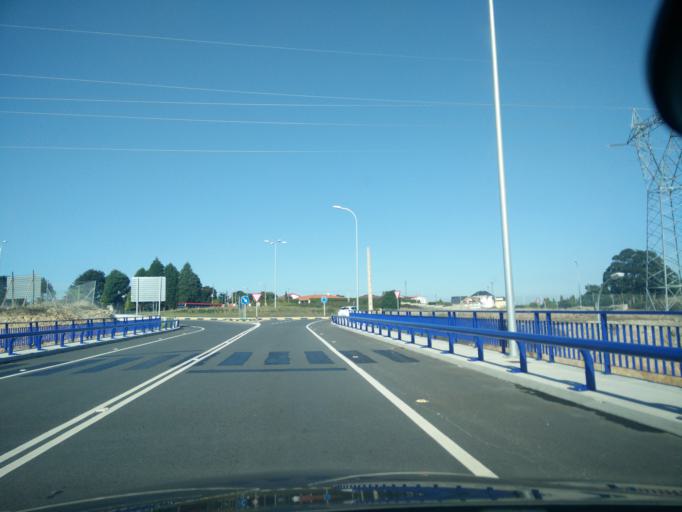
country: ES
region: Galicia
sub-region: Provincia da Coruna
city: Culleredo
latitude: 43.3226
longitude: -8.4097
